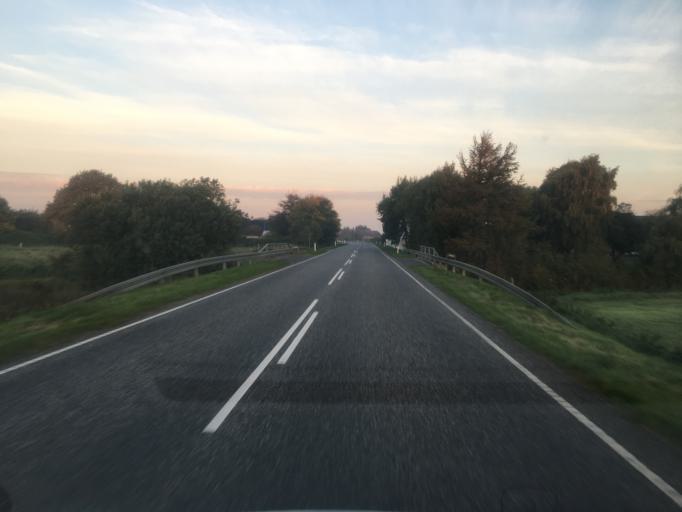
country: DK
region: South Denmark
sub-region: Tonder Kommune
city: Logumkloster
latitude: 55.0322
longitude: 9.0475
